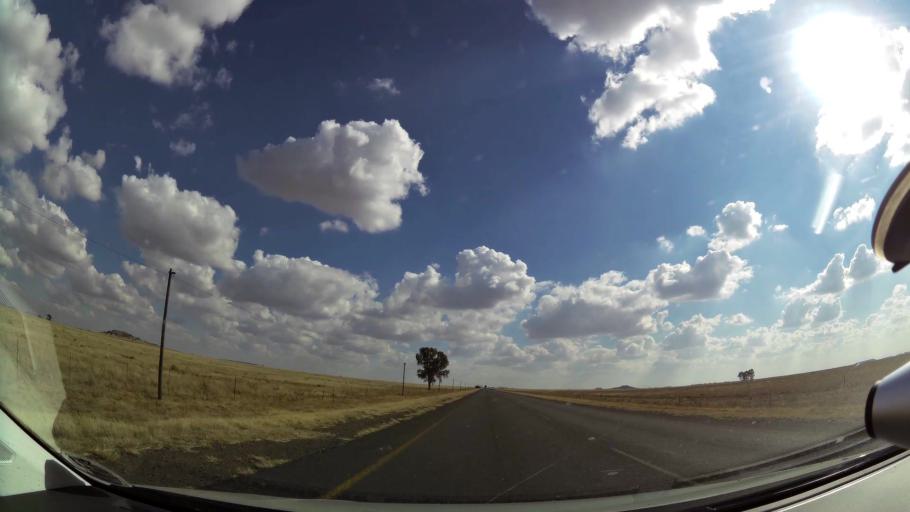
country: ZA
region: Orange Free State
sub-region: Mangaung Metropolitan Municipality
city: Bloemfontein
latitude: -29.1557
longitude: 25.7345
